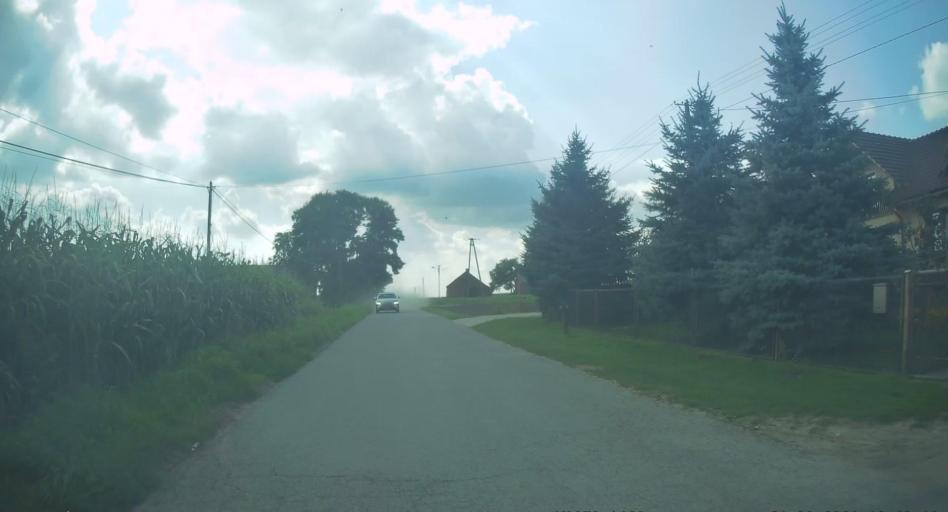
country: PL
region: Lesser Poland Voivodeship
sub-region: Powiat proszowicki
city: Nowe Brzesko
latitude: 50.1563
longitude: 20.4462
